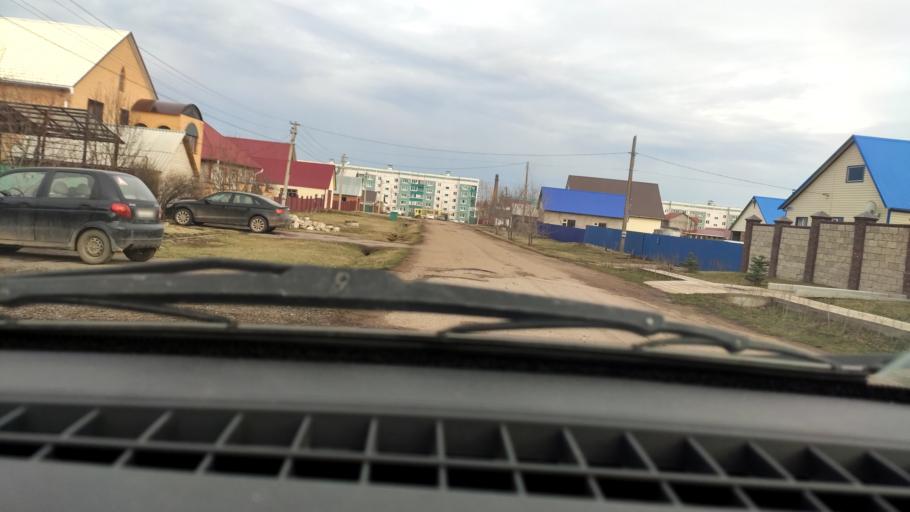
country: RU
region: Bashkortostan
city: Davlekanovo
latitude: 54.2302
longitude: 55.0305
